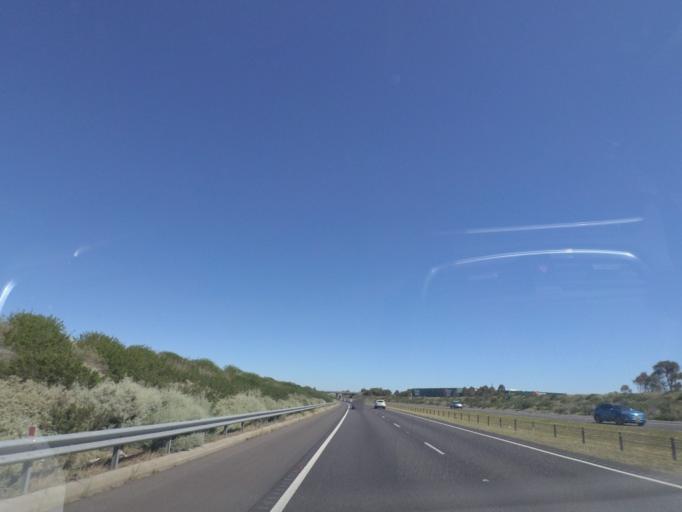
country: AU
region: Victoria
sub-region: Hume
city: Craigieburn
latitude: -37.5790
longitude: 144.9421
